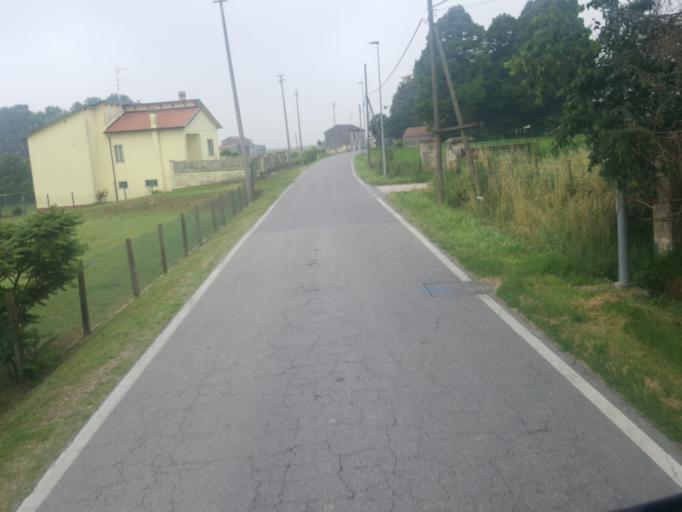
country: IT
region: Veneto
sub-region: Provincia di Rovigo
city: Canaro
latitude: 44.9334
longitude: 11.6631
